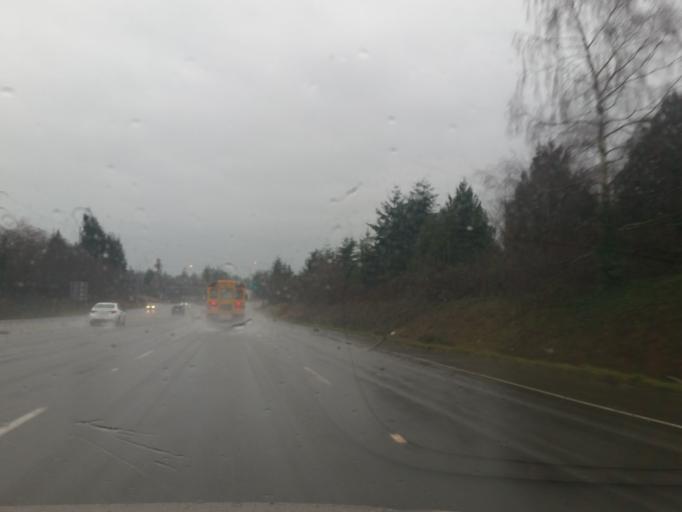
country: US
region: Washington
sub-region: Snohomish County
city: Mukilteo
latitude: 47.9273
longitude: -122.2608
